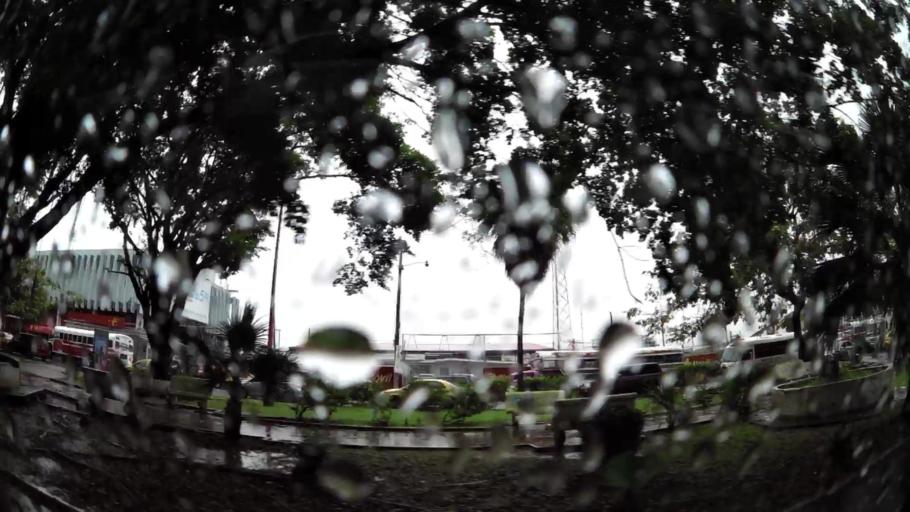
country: PA
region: Colon
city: Colon
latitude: 9.3533
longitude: -79.9004
